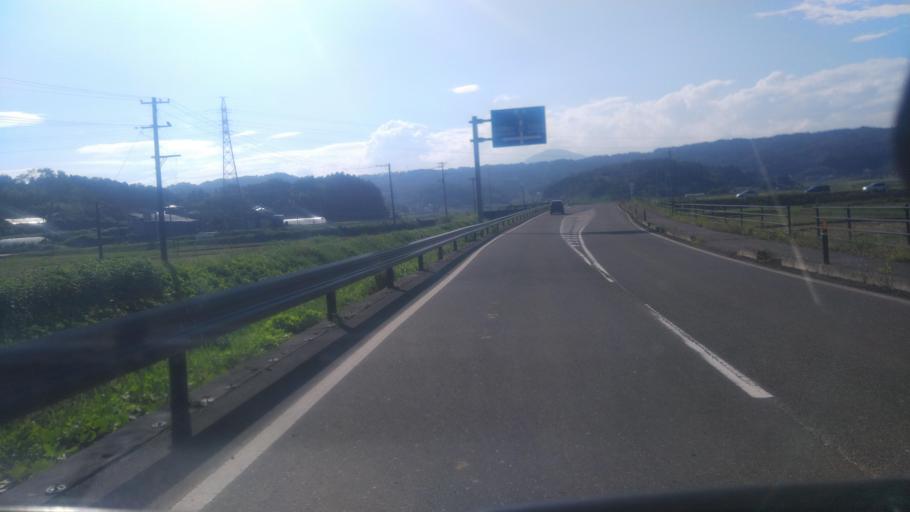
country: JP
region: Miyagi
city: Okawara
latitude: 38.0829
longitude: 140.7207
